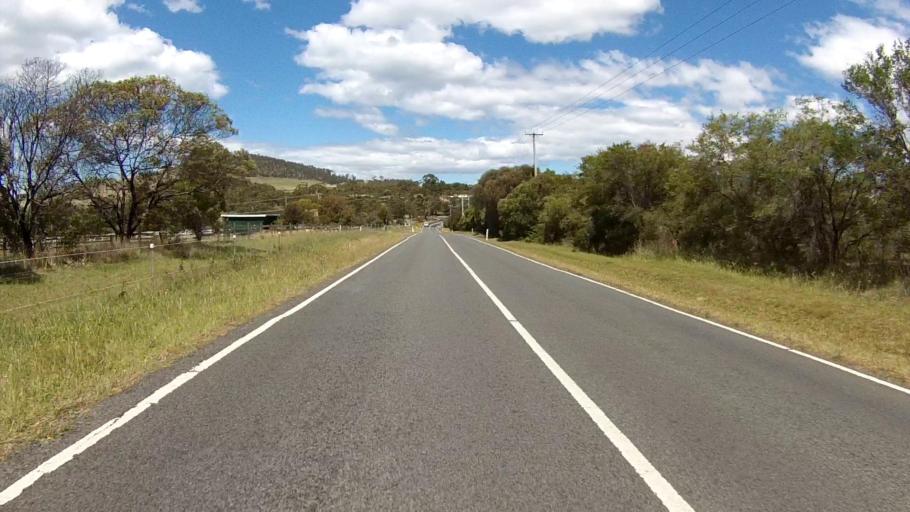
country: AU
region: Tasmania
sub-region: Clarence
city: Acton Park
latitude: -42.8654
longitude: 147.4815
